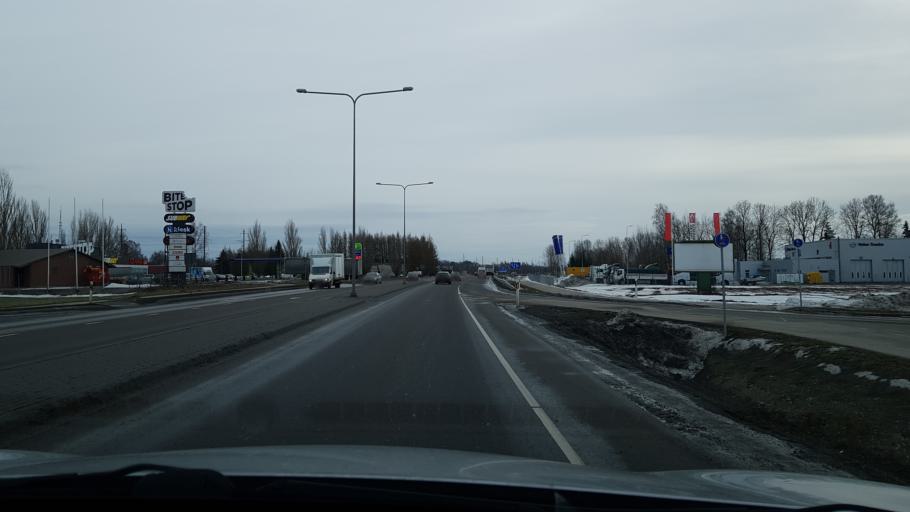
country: EE
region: Tartu
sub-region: Tartu linn
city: Tartu
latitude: 58.3768
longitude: 26.6770
